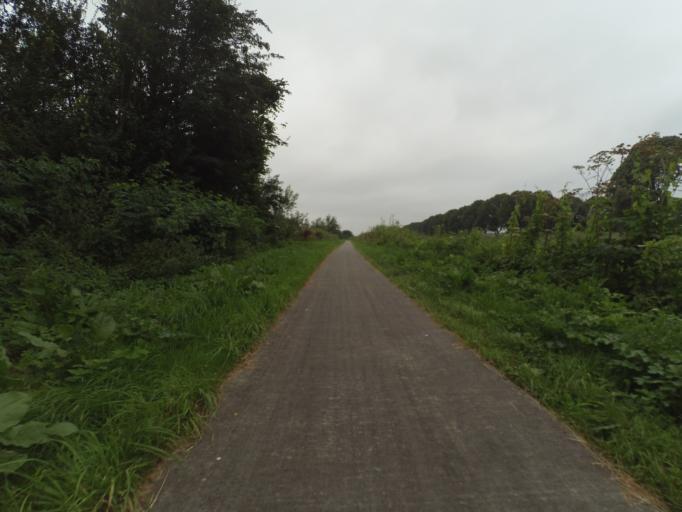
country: NL
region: Flevoland
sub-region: Gemeente Lelystad
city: Lelystad
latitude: 52.4611
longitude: 5.5342
